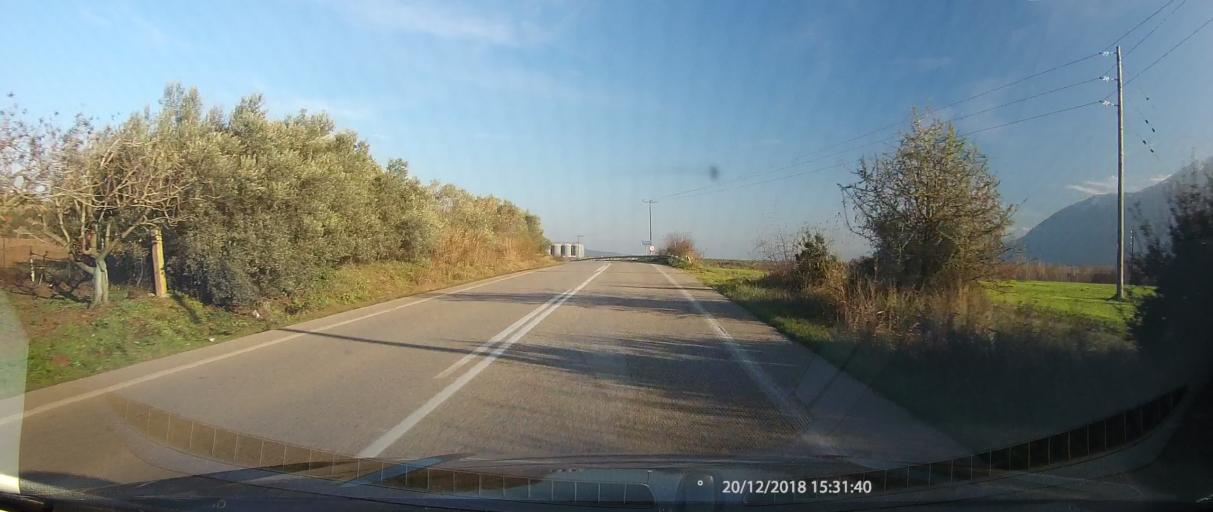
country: GR
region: Central Greece
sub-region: Nomos Fthiotidos
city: Lianokladhion
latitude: 38.9299
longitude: 22.2437
